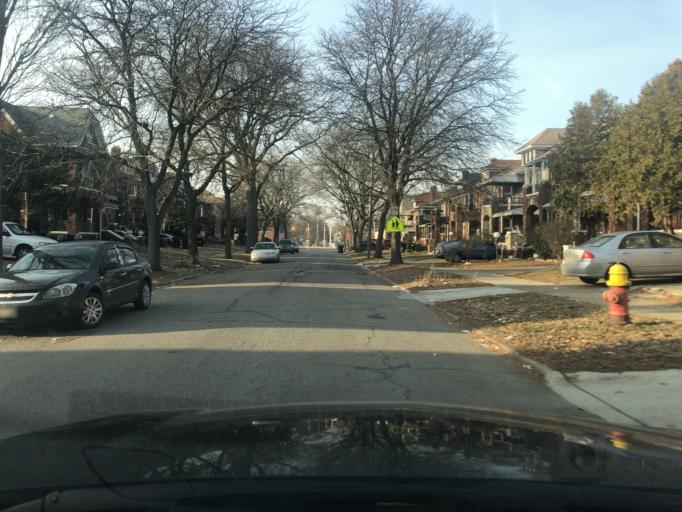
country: US
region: Michigan
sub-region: Wayne County
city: Highland Park
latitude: 42.3861
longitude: -83.1258
